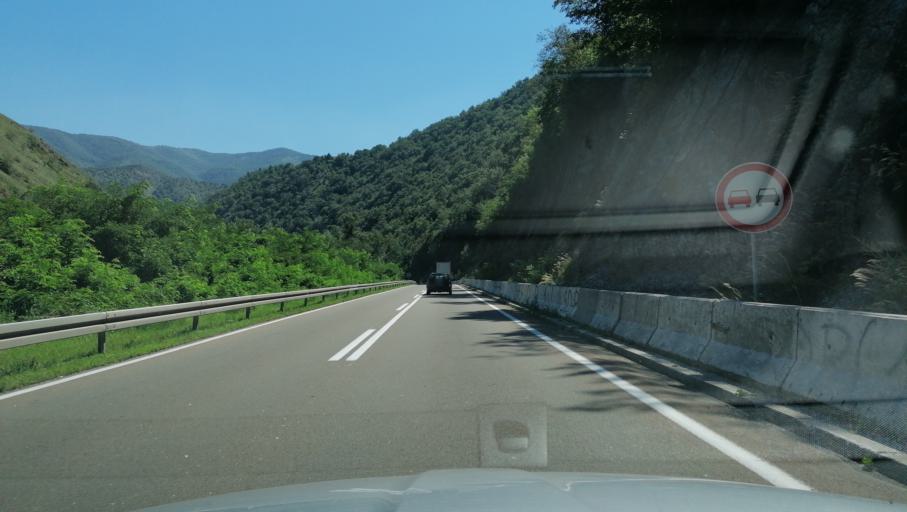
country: RS
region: Central Serbia
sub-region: Raski Okrug
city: Kraljevo
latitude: 43.5636
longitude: 20.6046
